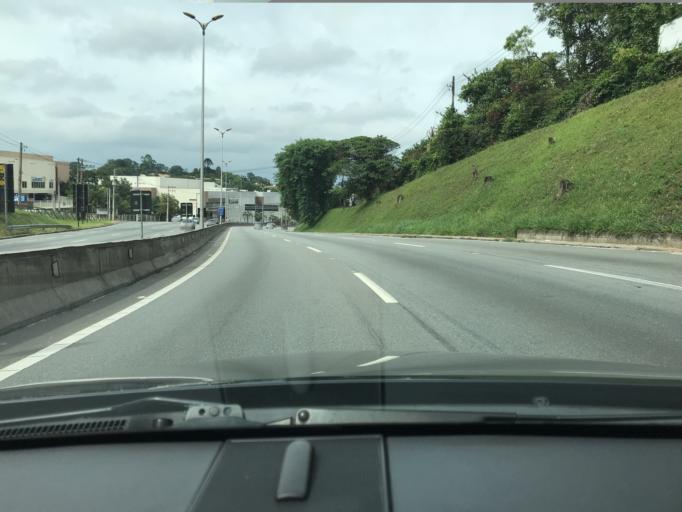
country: BR
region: Sao Paulo
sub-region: Taboao Da Serra
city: Taboao da Serra
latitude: -23.5897
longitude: -46.8308
